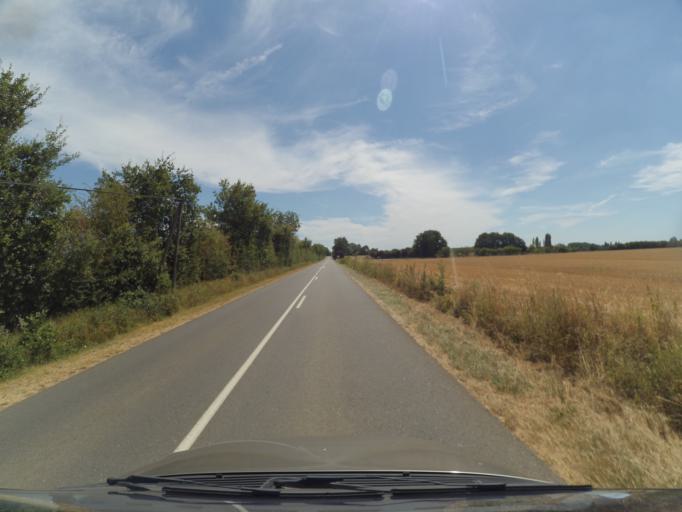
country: FR
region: Poitou-Charentes
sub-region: Departement de la Vienne
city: Usson-du-Poitou
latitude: 46.2282
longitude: 0.5290
